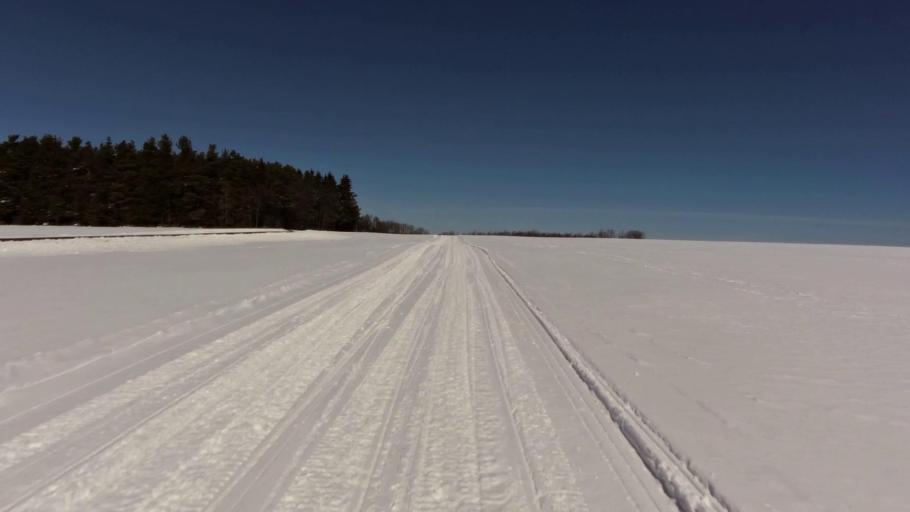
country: US
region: New York
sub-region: Allegany County
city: Houghton
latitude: 42.3550
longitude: -78.2607
